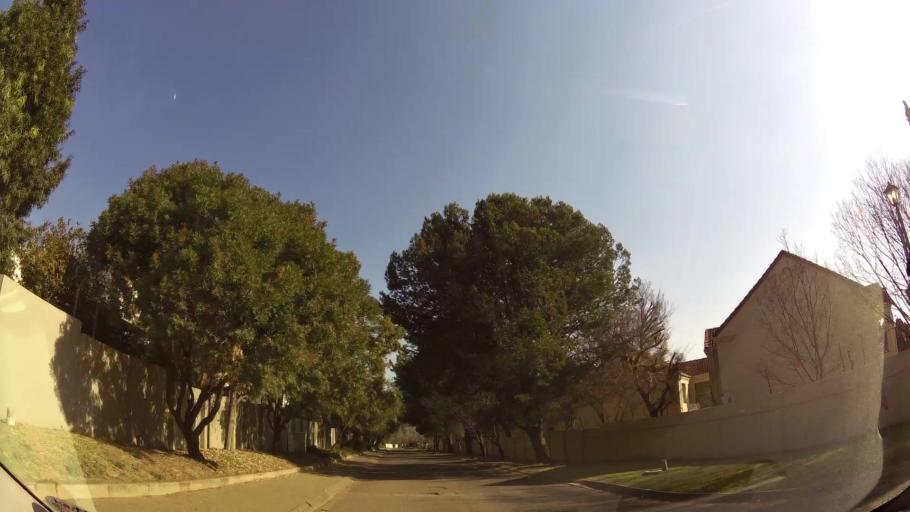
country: ZA
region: Gauteng
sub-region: City of Johannesburg Metropolitan Municipality
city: Diepsloot
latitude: -26.0673
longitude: 28.0129
